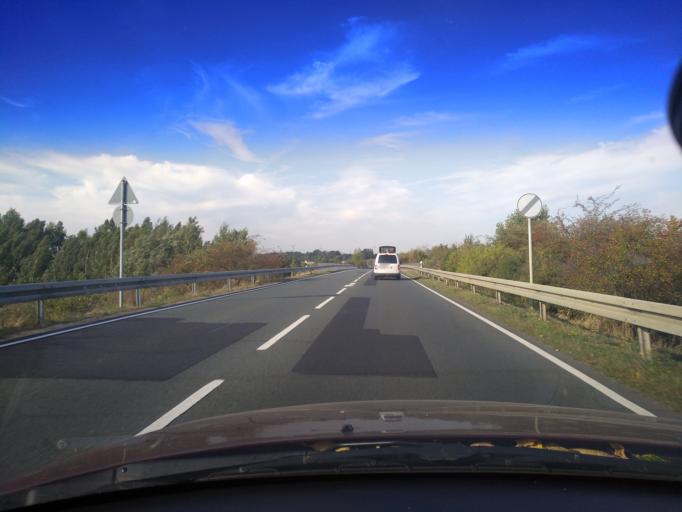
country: DE
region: Saxony
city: Goerlitz
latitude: 51.1721
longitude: 14.9593
